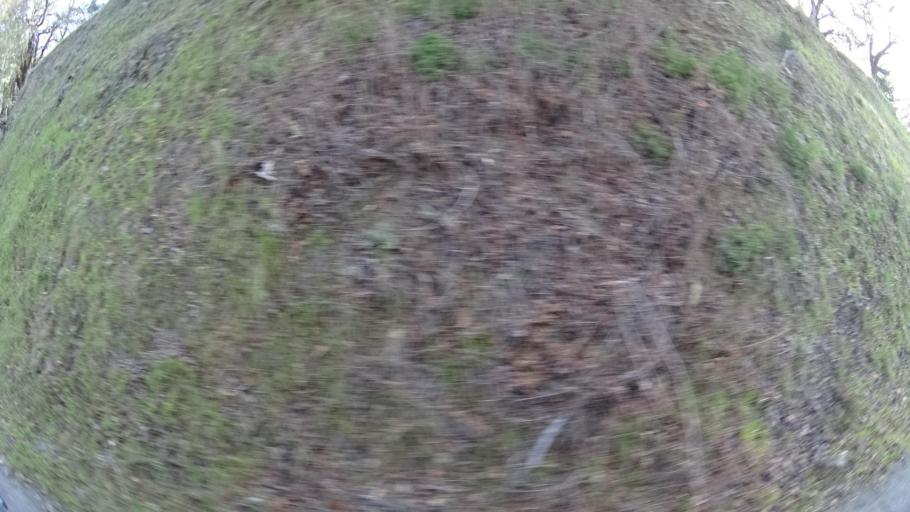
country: US
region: California
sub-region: Humboldt County
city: Hydesville
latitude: 40.6403
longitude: -123.9040
